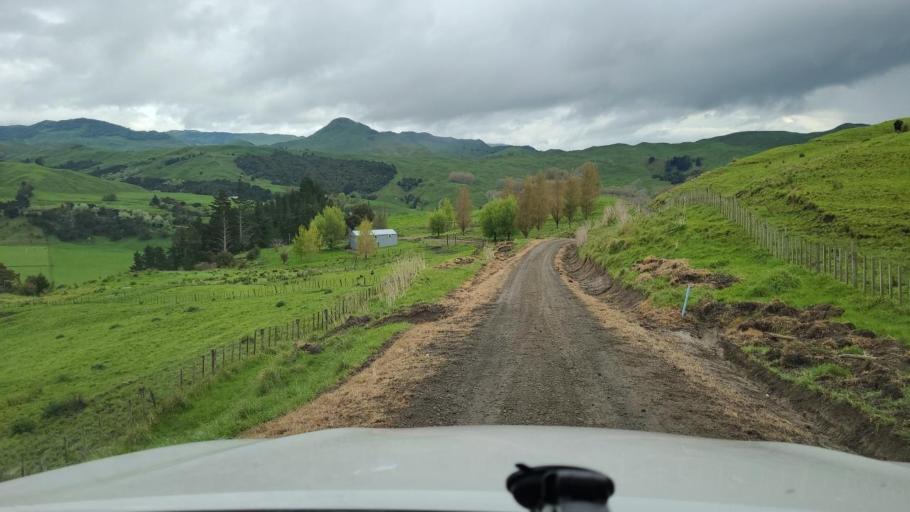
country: NZ
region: Gisborne
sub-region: Gisborne District
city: Gisborne
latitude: -38.4352
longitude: 177.7144
